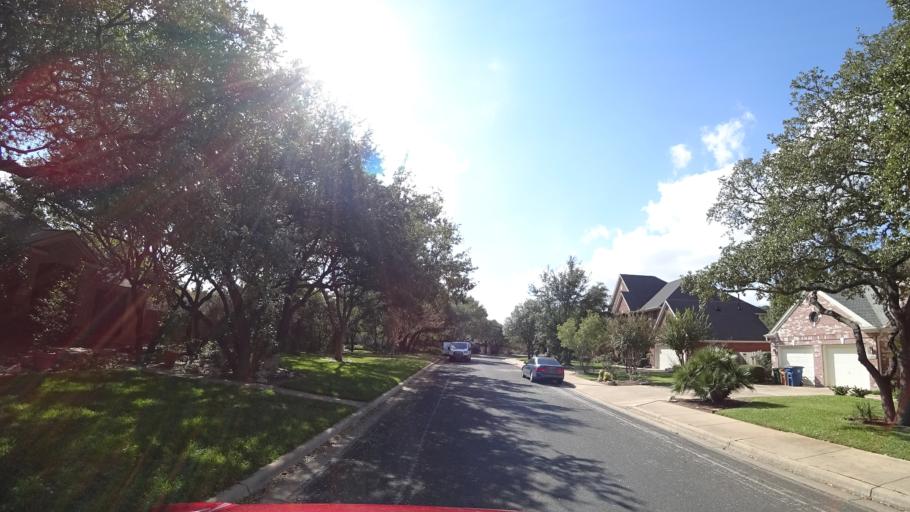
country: US
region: Texas
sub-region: Williamson County
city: Jollyville
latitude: 30.4179
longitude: -97.7872
